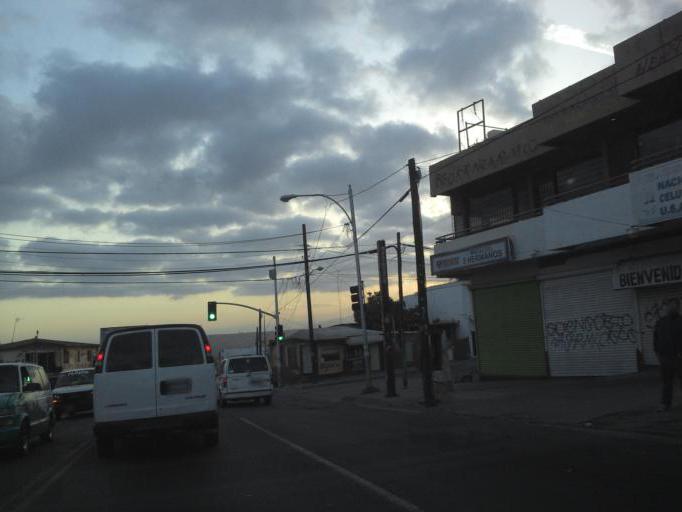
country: MX
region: Baja California
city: Tijuana
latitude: 32.5335
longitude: -117.0596
